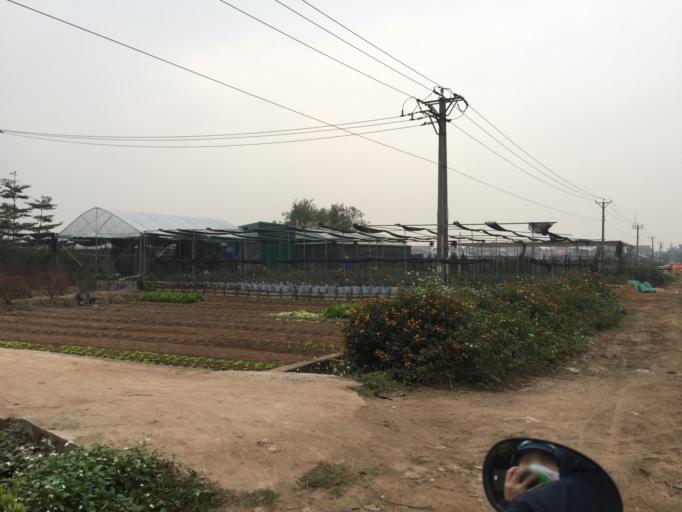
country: VN
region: Hung Yen
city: Van Giang
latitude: 20.9657
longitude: 105.9101
